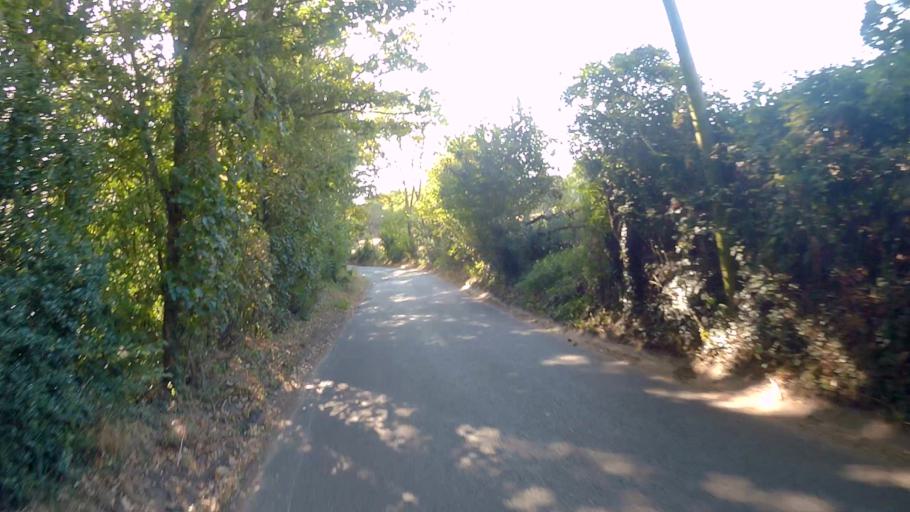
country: GB
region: England
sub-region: Surrey
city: Churt
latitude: 51.1763
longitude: -0.7841
